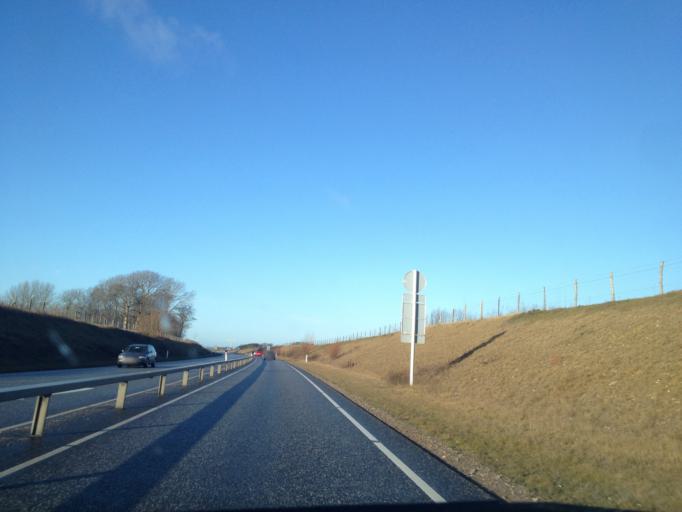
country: DK
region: Zealand
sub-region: Holbaek Kommune
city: Holbaek
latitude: 55.7307
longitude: 11.6209
